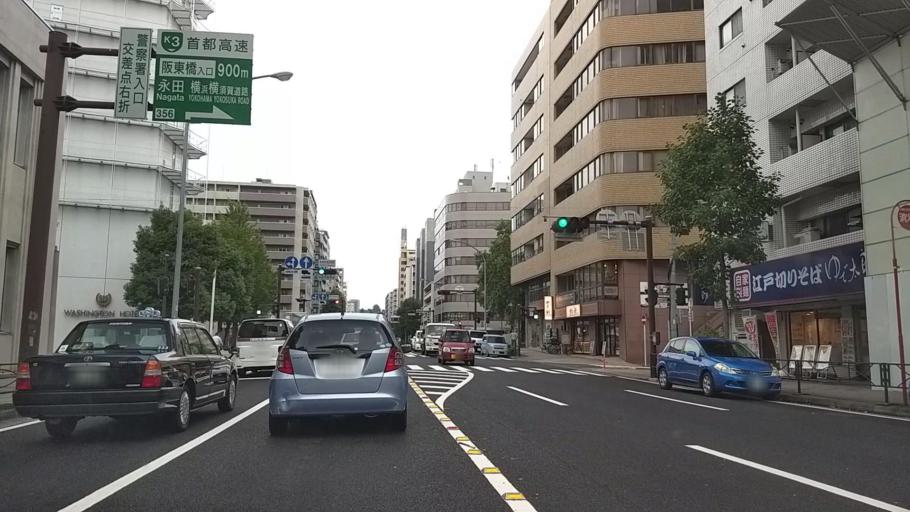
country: JP
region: Kanagawa
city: Yokohama
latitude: 35.4417
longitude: 139.6321
